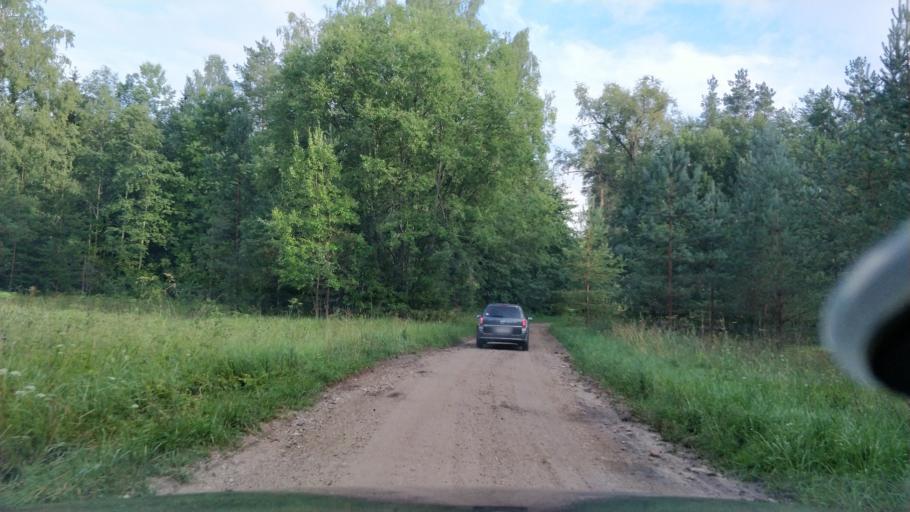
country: LV
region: Incukalns
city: Incukalns
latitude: 57.0980
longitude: 24.7762
